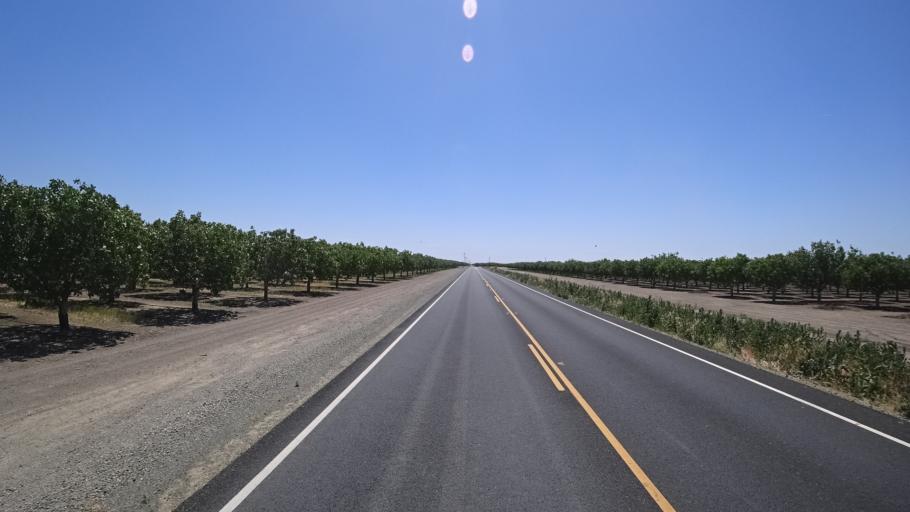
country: US
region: California
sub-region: Kings County
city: Corcoran
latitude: 36.1007
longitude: -119.5362
